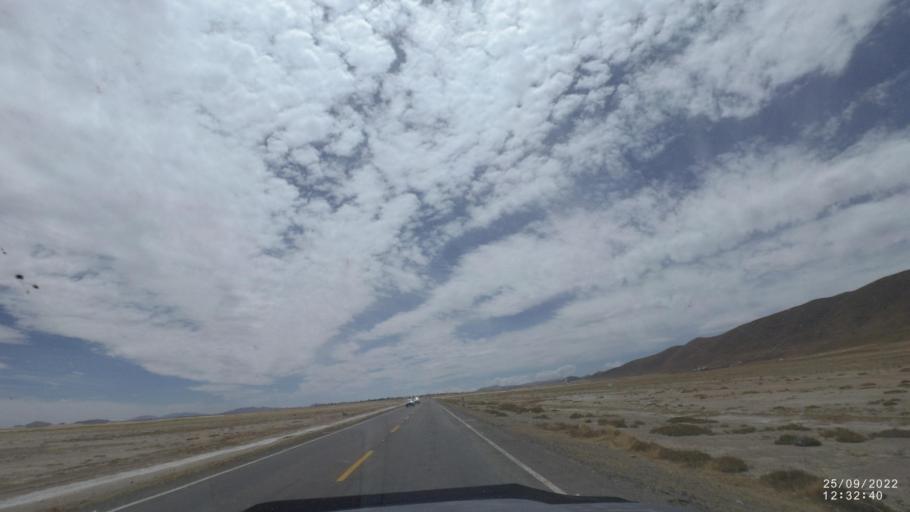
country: BO
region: Oruro
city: Machacamarca
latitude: -18.2077
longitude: -67.0104
